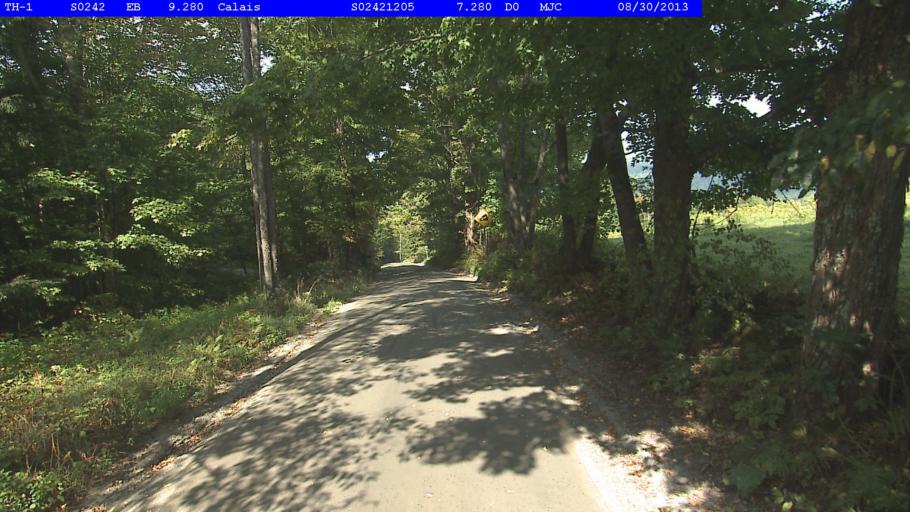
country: US
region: Vermont
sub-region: Caledonia County
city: Hardwick
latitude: 44.4024
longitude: -72.4323
